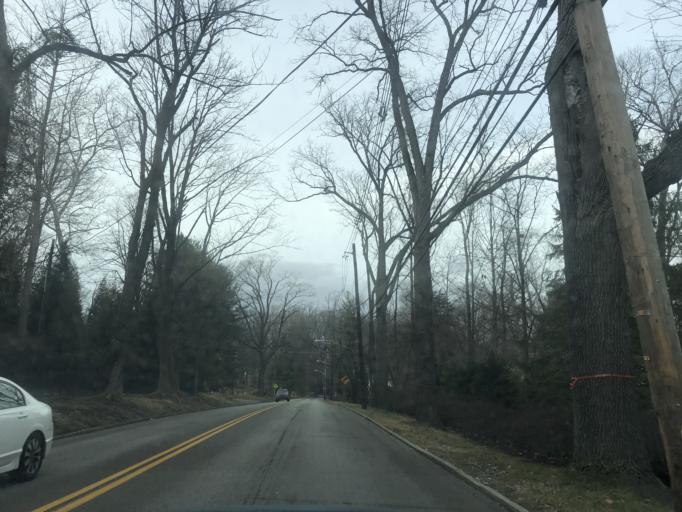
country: US
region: Pennsylvania
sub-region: Delaware County
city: Radnor
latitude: 40.0477
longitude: -75.3365
